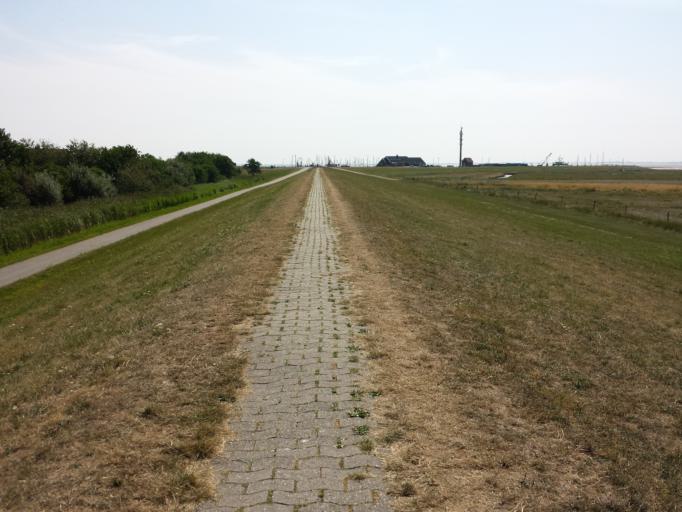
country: DE
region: Lower Saxony
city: Spiekeroog
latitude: 53.7685
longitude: 7.6904
